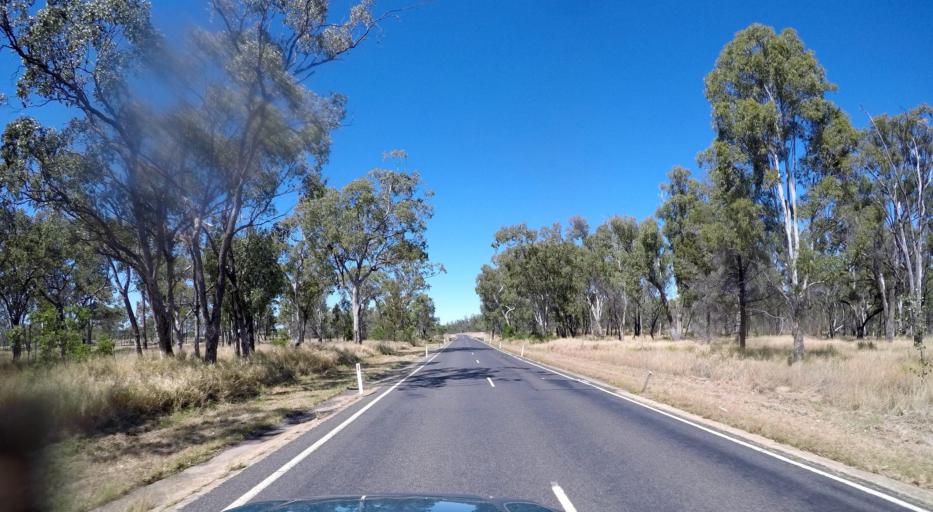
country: AU
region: Queensland
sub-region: Western Downs
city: Westcourt
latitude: -26.5437
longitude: 150.1405
